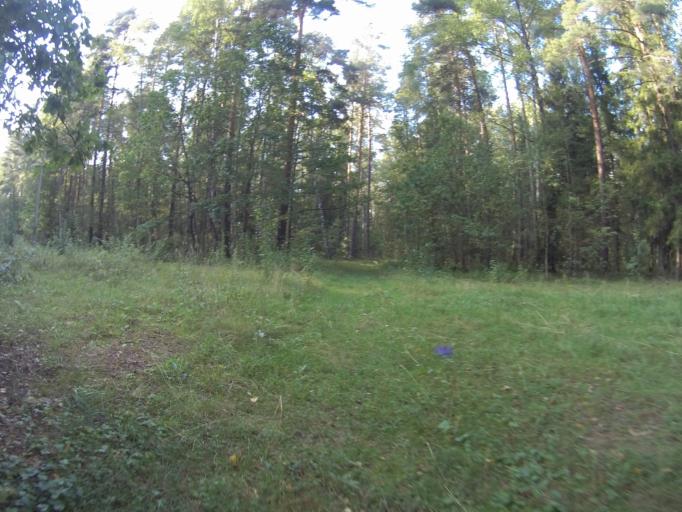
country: RU
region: Vladimir
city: Kommunar
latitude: 56.0609
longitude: 40.4626
